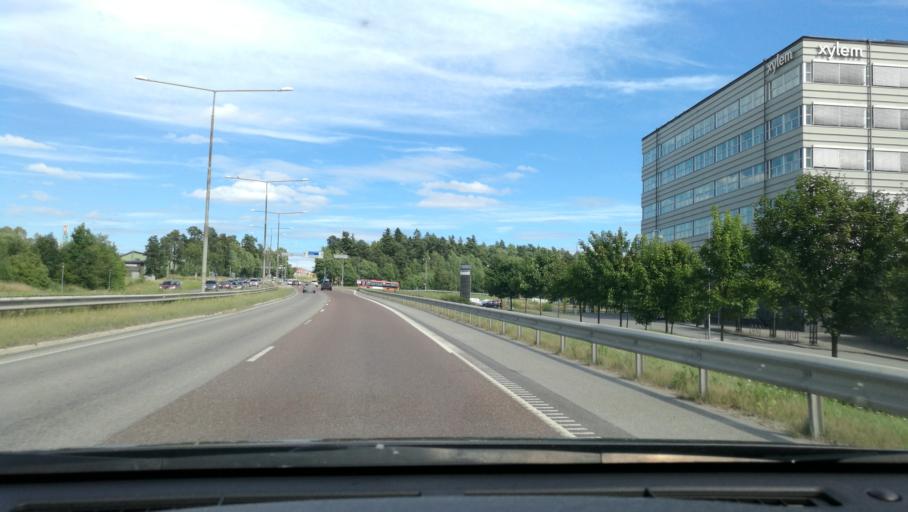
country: SE
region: Stockholm
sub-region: Sundbybergs Kommun
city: Sundbyberg
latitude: 59.3798
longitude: 17.9667
